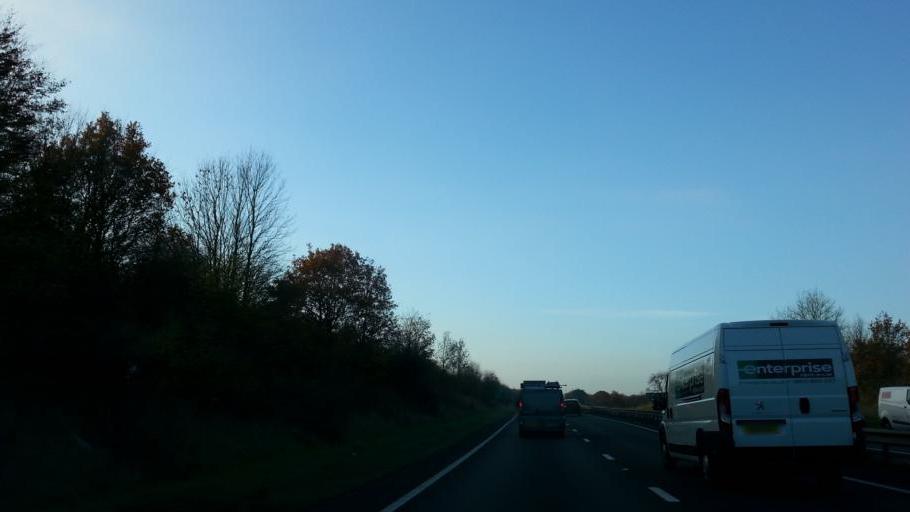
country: GB
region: England
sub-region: Leicestershire
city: Measham
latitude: 52.7211
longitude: -1.4963
